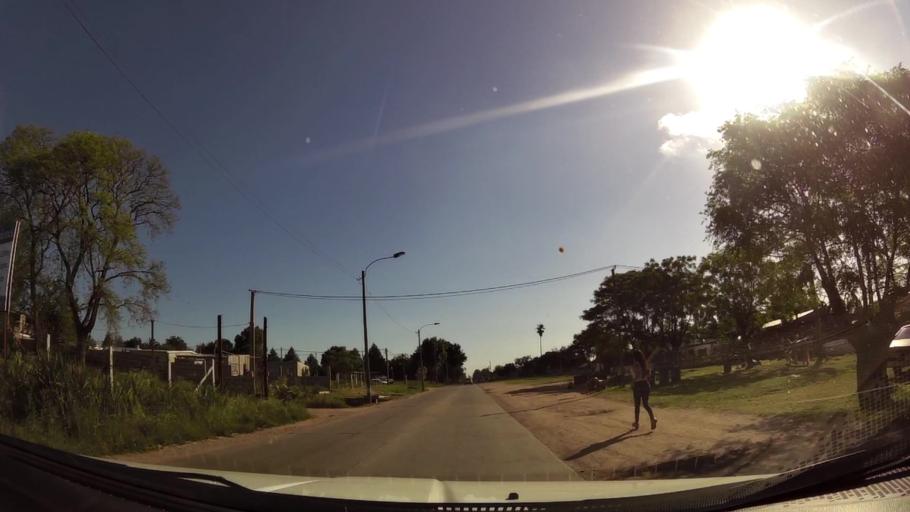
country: UY
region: Canelones
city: La Paz
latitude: -34.8174
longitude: -56.1732
